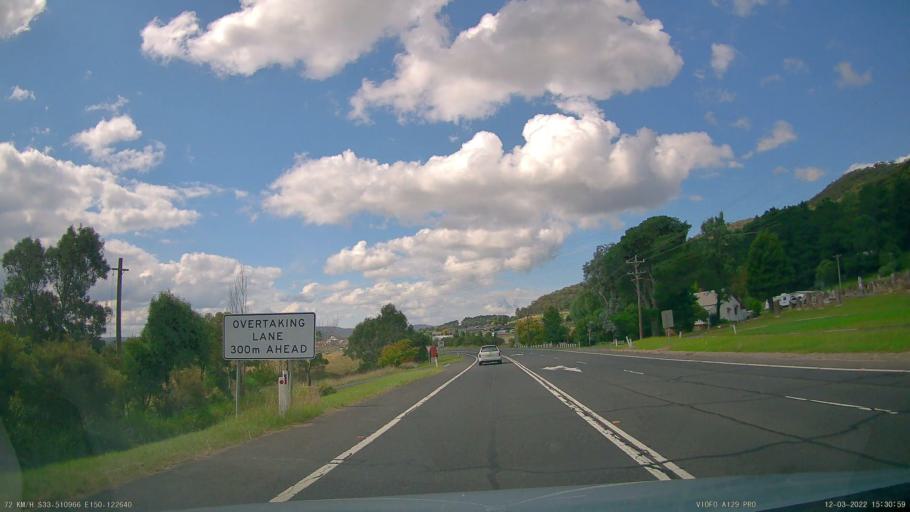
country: AU
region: New South Wales
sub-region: Lithgow
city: Bowenfels
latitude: -33.5107
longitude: 150.1229
